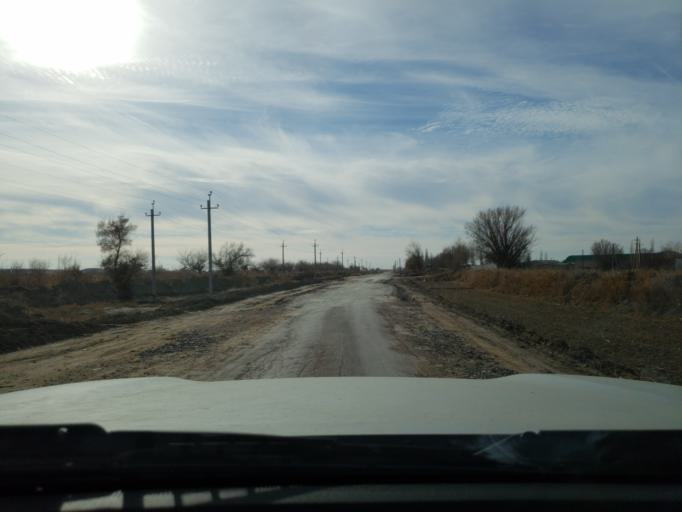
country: TM
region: Dasoguz
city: Dasoguz
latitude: 41.8476
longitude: 59.8794
